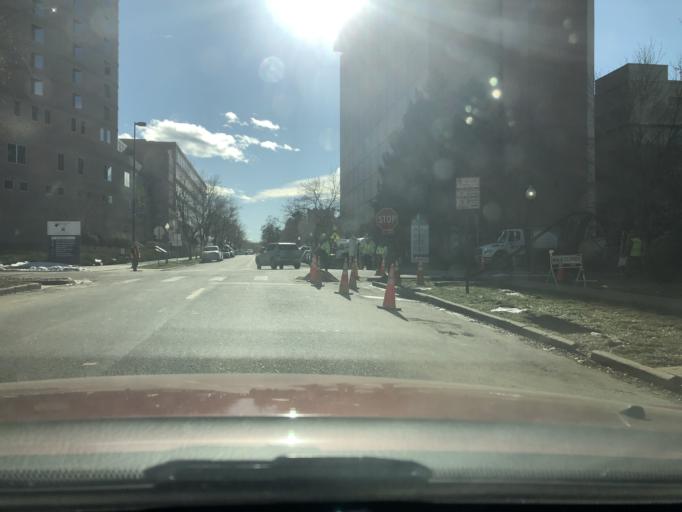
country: US
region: Colorado
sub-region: Denver County
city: Denver
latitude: 39.7485
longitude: -104.9684
